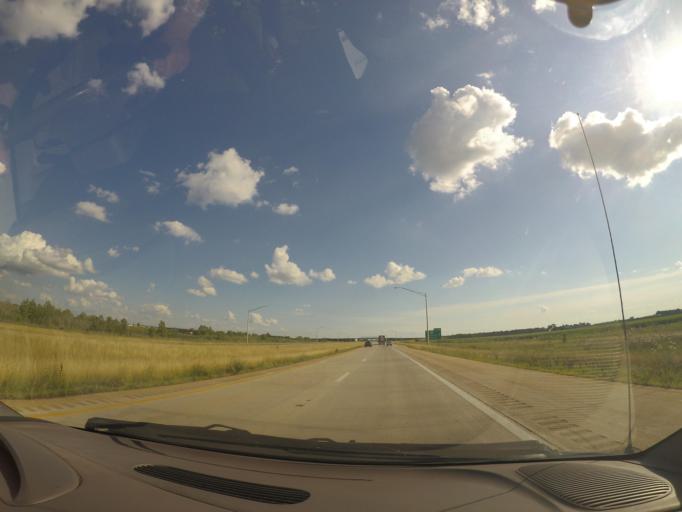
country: US
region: Ohio
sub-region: Lucas County
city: Waterville
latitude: 41.5144
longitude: -83.7508
